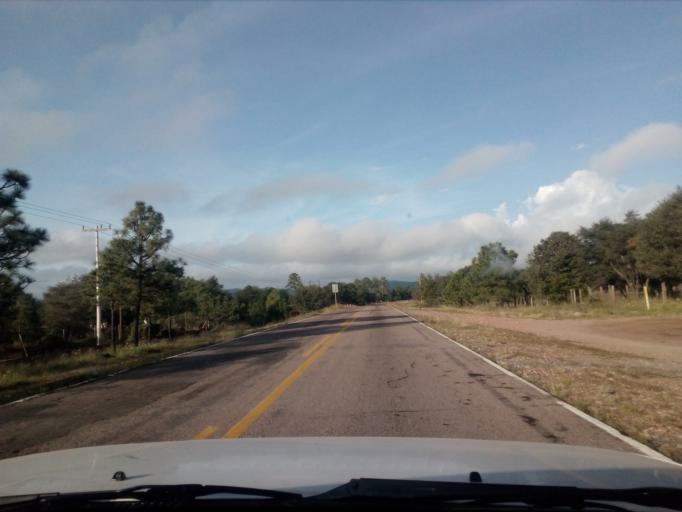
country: MX
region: Durango
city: Victoria de Durango
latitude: 23.9280
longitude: -104.9274
